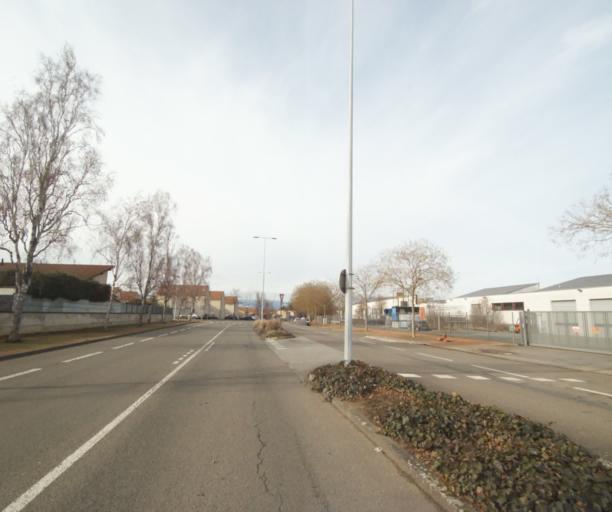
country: FR
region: Rhone-Alpes
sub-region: Departement de la Loire
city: Riorges
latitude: 46.0264
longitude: 4.0516
